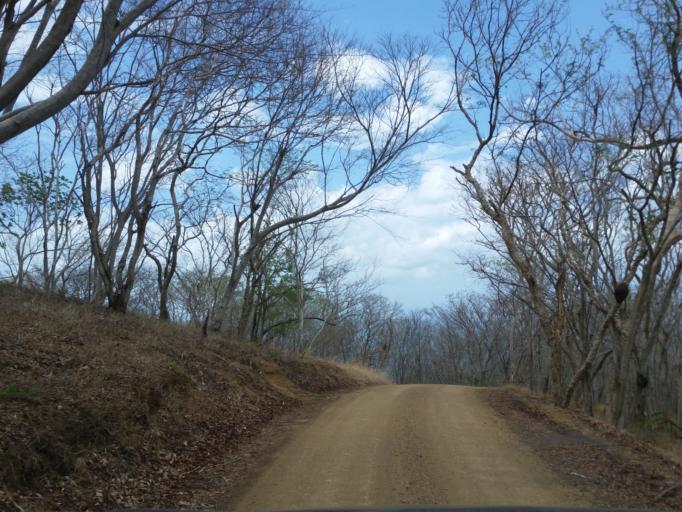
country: NI
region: Rivas
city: Tola
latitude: 11.4183
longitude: -86.0670
